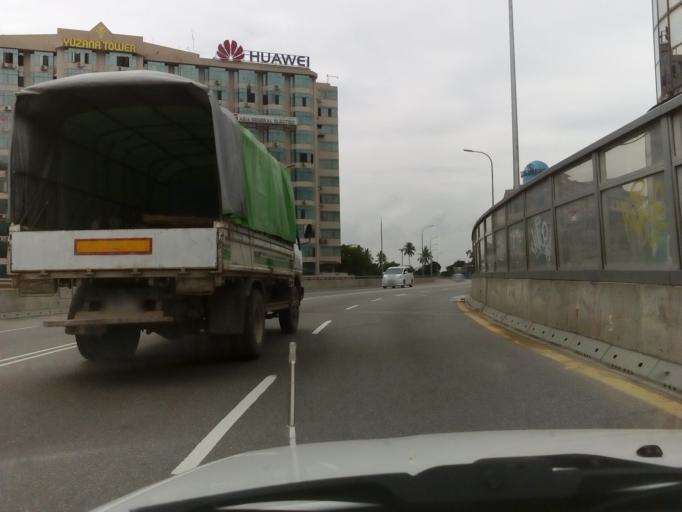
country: MM
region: Yangon
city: Yangon
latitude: 16.8056
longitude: 96.1557
